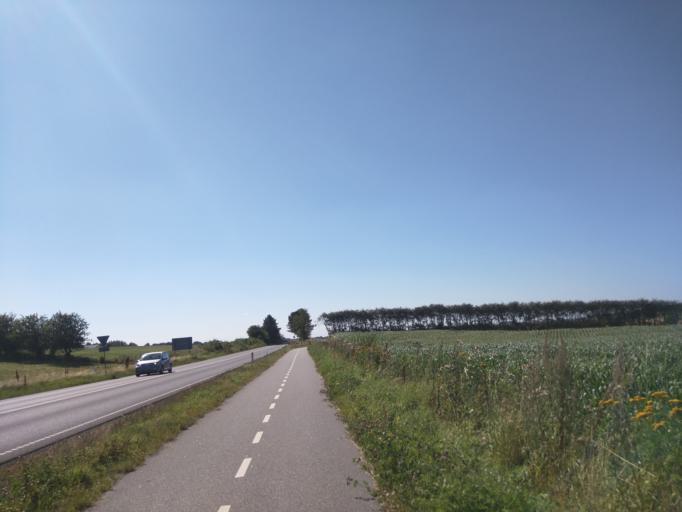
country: DK
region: Central Jutland
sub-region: Viborg Kommune
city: Viborg
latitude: 56.4640
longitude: 9.4986
